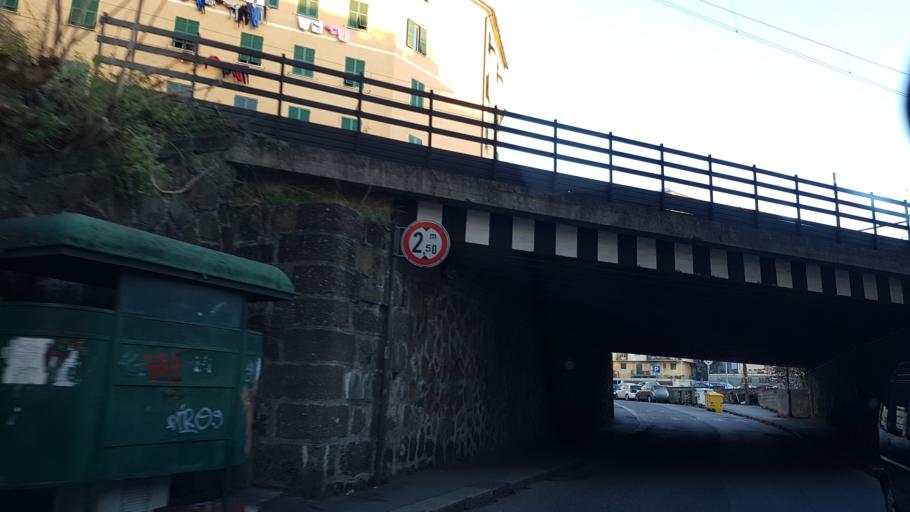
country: IT
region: Liguria
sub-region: Provincia di Genova
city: Genoa
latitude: 44.4330
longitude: 8.8933
